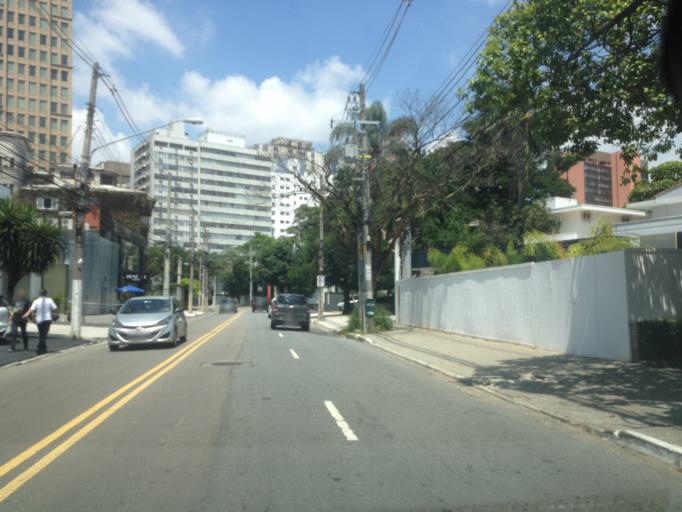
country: BR
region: Sao Paulo
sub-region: Sao Paulo
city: Sao Paulo
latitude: -23.5741
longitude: -46.6855
